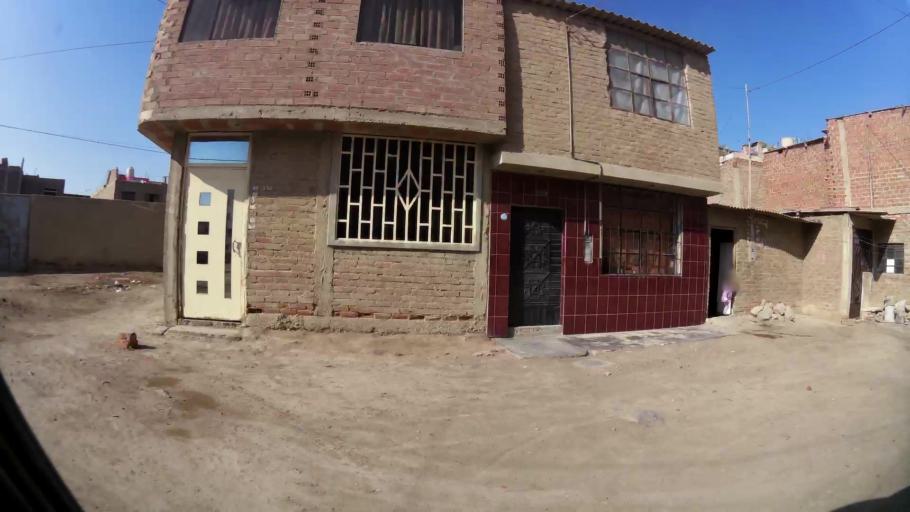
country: PE
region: Lambayeque
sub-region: Provincia de Chiclayo
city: Chiclayo
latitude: -6.7669
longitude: -79.8467
